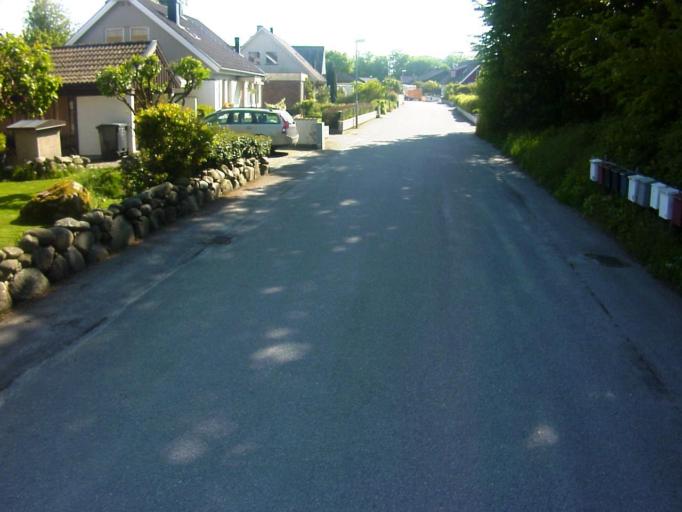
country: SE
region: Blekinge
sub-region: Solvesborgs Kommun
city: Soelvesborg
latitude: 56.0123
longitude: 14.6923
